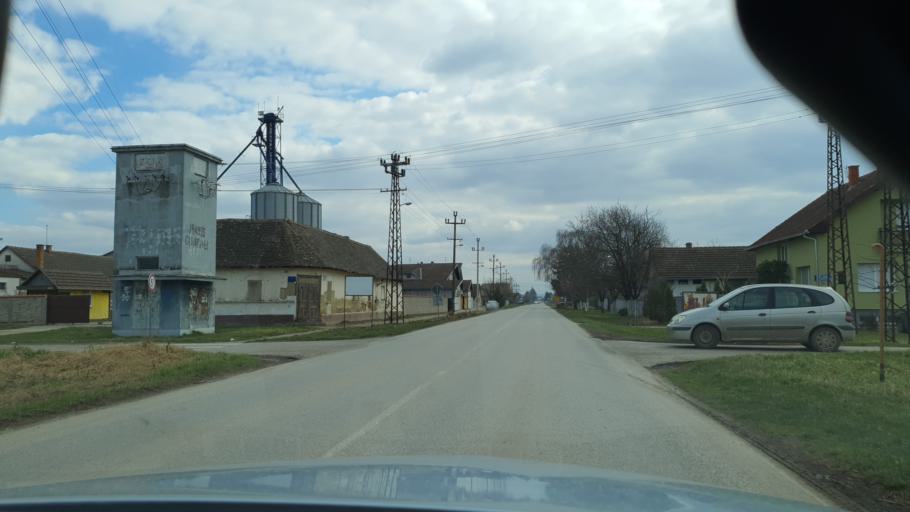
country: RS
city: Maglic
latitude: 45.3963
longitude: 19.4556
